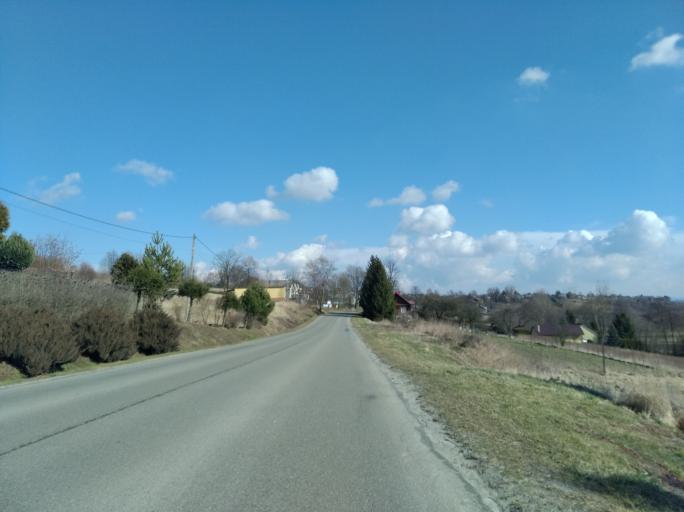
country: PL
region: Subcarpathian Voivodeship
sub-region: Powiat strzyzowski
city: Frysztak
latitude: 49.8446
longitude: 21.5762
